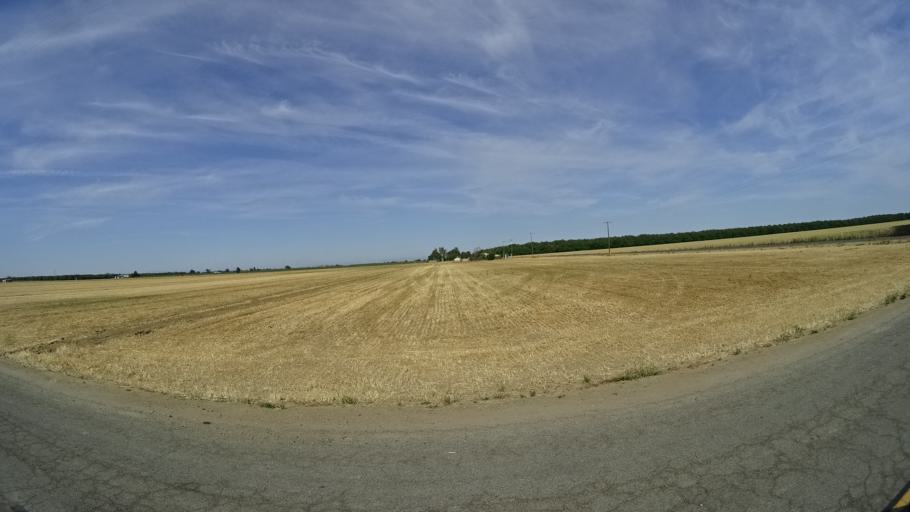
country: US
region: California
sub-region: Kings County
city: Lucerne
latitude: 36.3861
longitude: -119.6100
